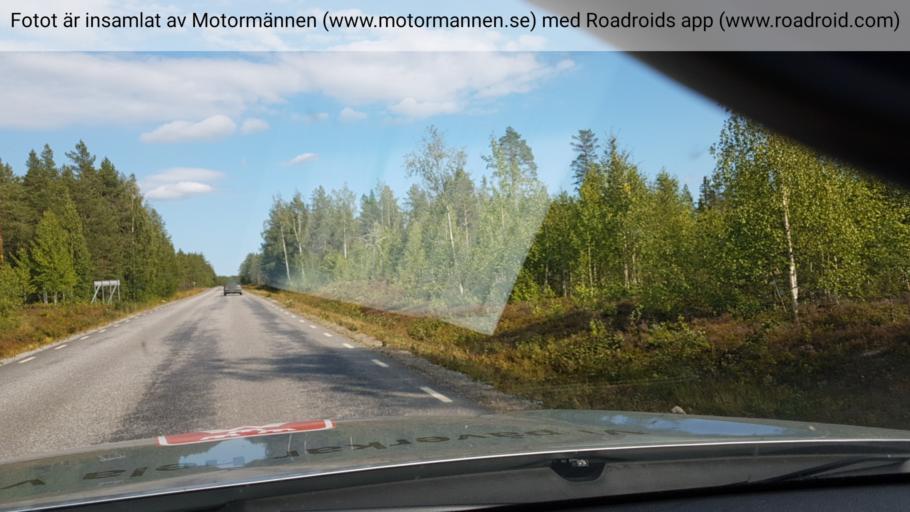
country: SE
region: Norrbotten
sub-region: Pitea Kommun
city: Roknas
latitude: 65.2009
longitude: 21.1583
